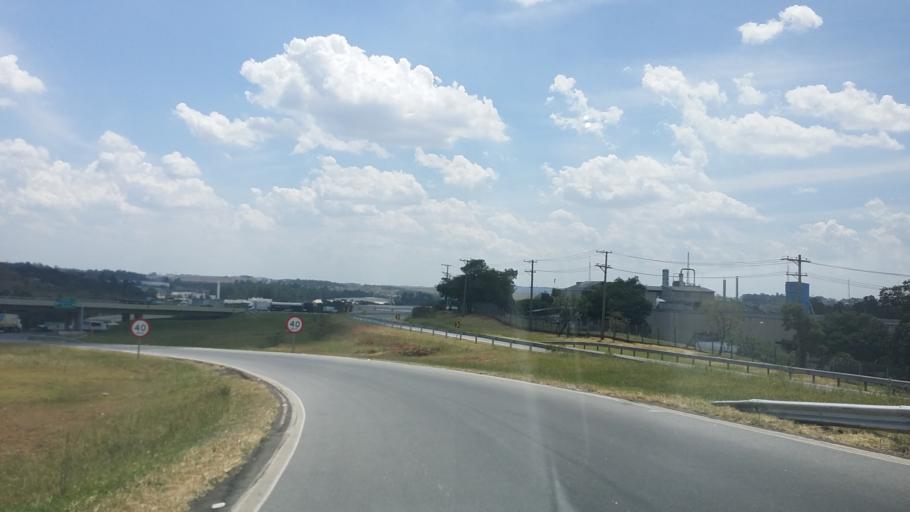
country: BR
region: Sao Paulo
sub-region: Jundiai
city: Jundiai
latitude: -23.1717
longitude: -46.9360
